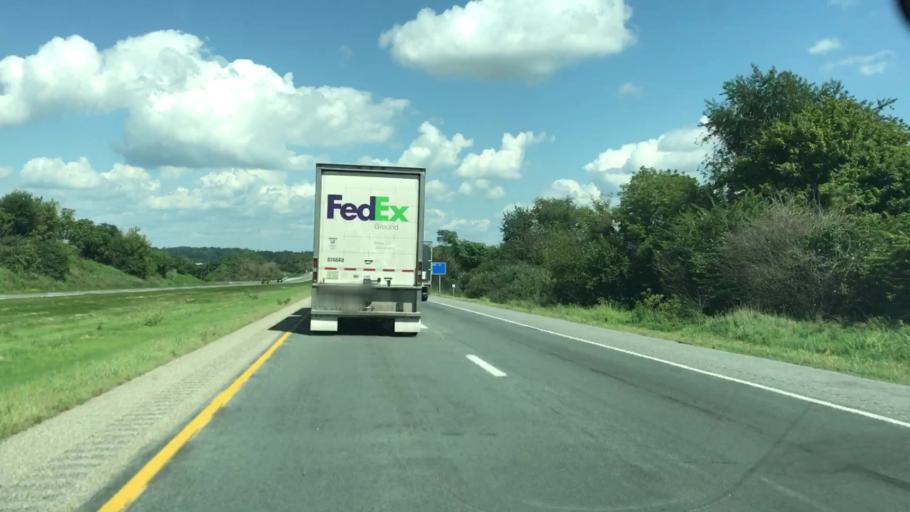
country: US
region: Pennsylvania
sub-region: Cumberland County
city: Newville
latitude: 40.1245
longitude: -77.3566
